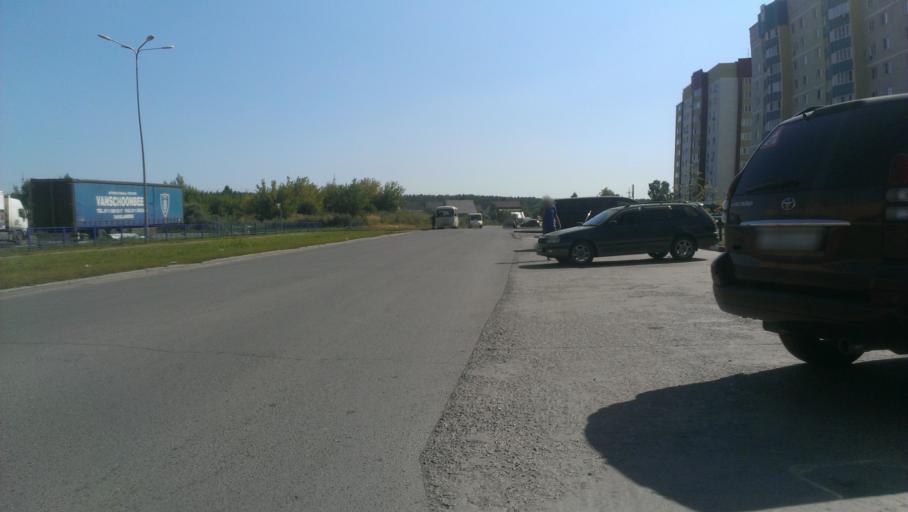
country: RU
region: Altai Krai
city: Novosilikatnyy
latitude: 53.3265
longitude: 83.6832
